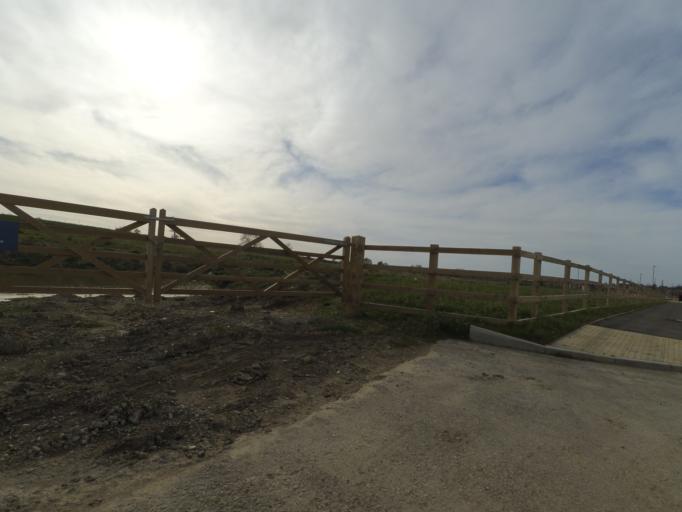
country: GB
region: England
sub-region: Warwickshire
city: Rugby
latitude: 52.3660
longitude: -1.2025
